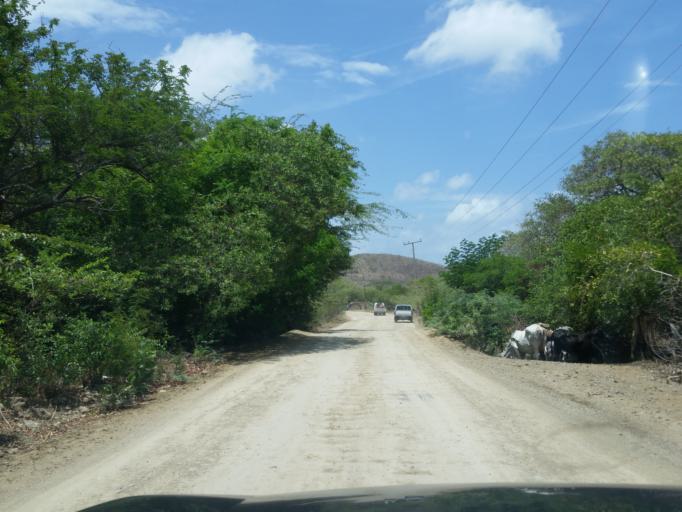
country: NI
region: Rivas
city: Tola
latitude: 11.4682
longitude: -86.1002
